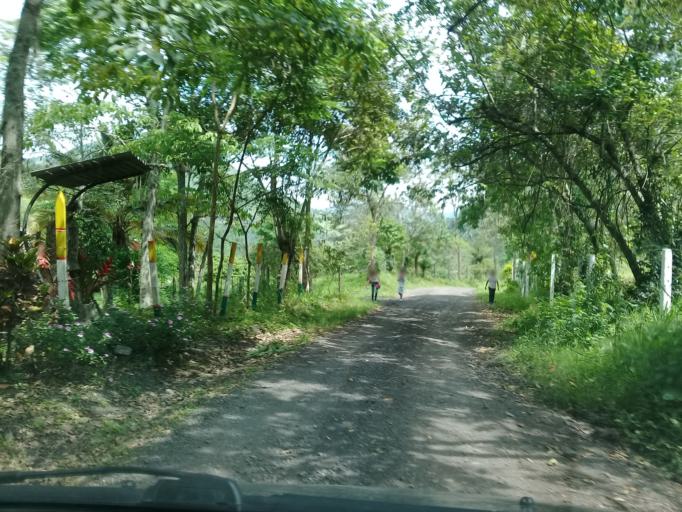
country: CO
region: Cundinamarca
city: Viani
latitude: 4.8600
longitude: -74.5416
